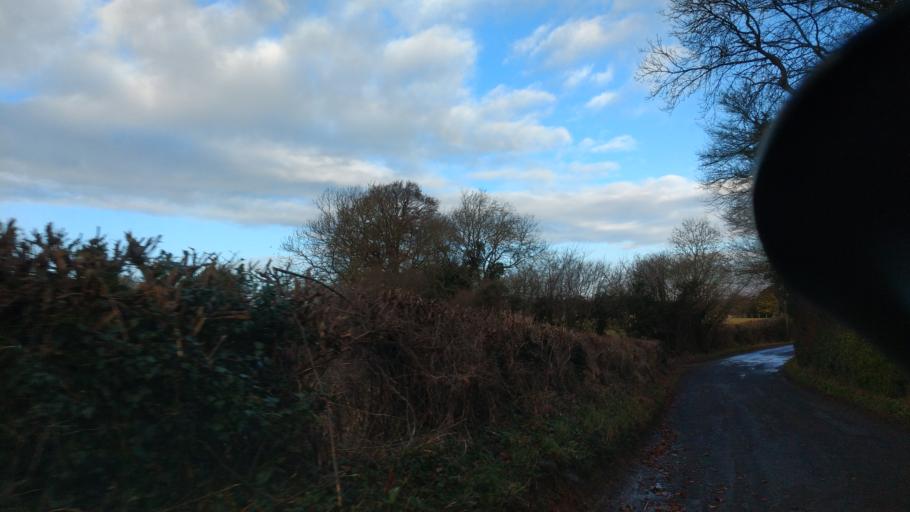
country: GB
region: England
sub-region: Wiltshire
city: Corsham
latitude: 51.4482
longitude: -2.1752
